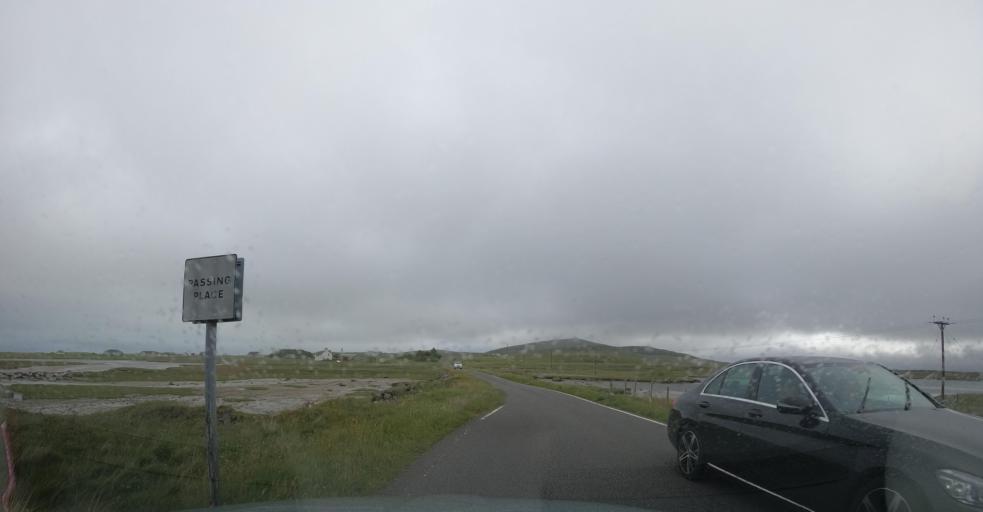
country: GB
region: Scotland
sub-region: Eilean Siar
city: Isle of North Uist
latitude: 57.6532
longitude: -7.2467
